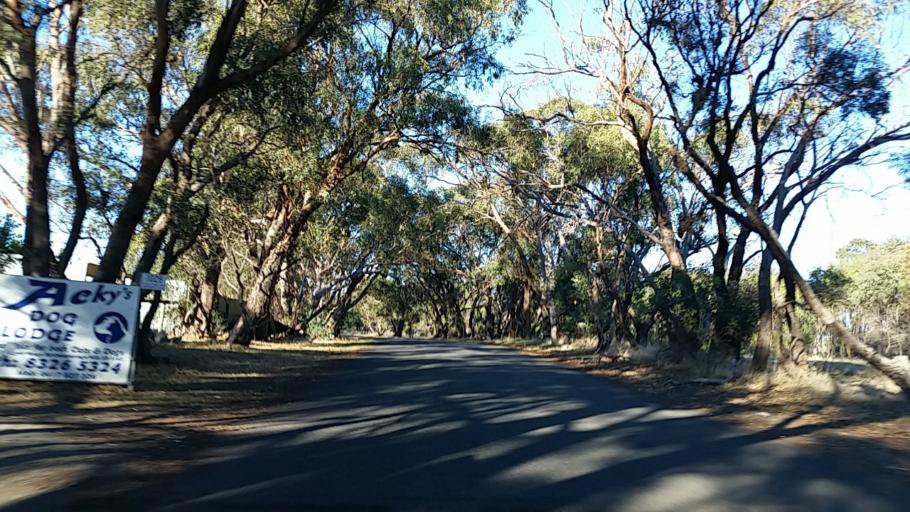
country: AU
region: South Australia
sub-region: Onkaparinga
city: Hackham
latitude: -35.1540
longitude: 138.5520
